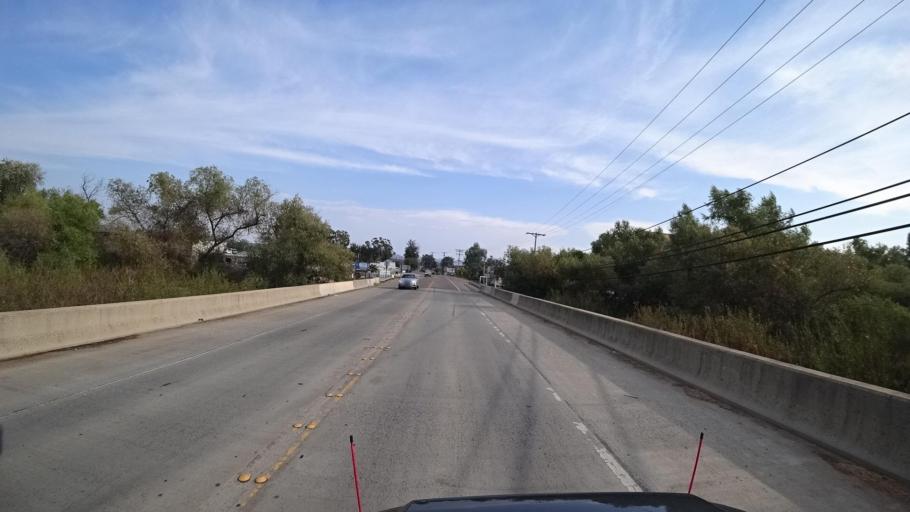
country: US
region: California
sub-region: San Diego County
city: Ramona
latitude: 33.0453
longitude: -116.8708
